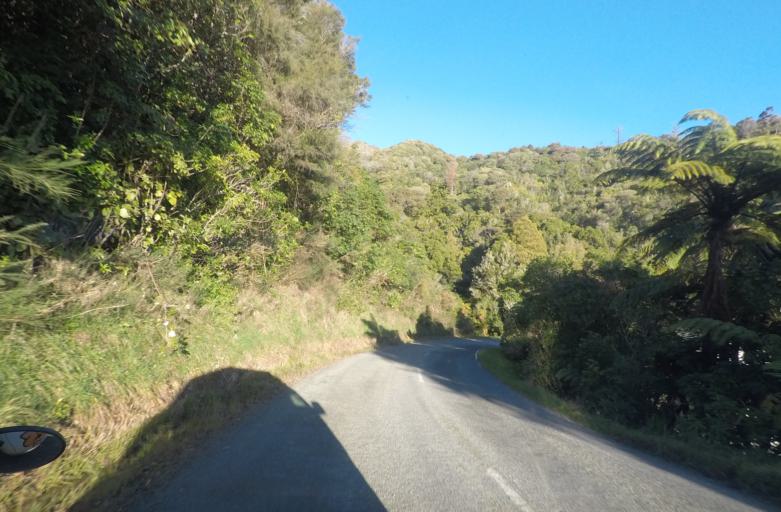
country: NZ
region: Marlborough
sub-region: Marlborough District
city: Picton
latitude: -41.2732
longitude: 173.9697
